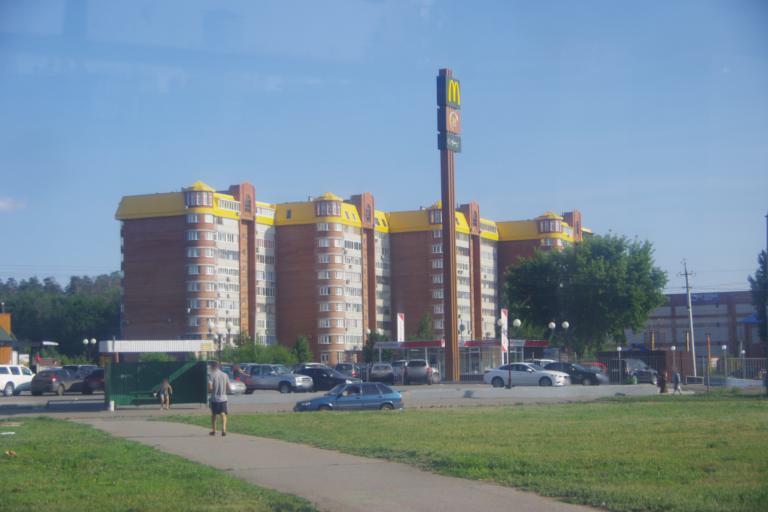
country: RU
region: Samara
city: Tol'yatti
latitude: 53.5179
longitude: 49.3115
